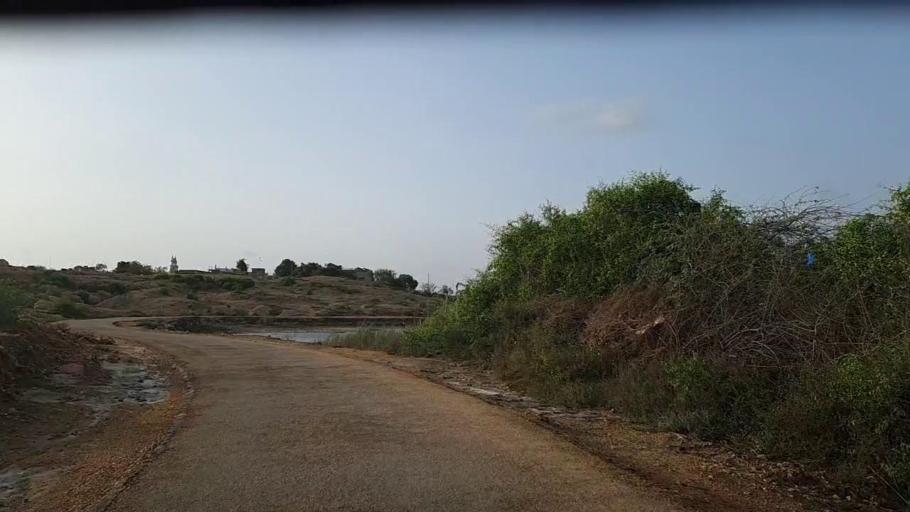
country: PK
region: Sindh
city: Thatta
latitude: 24.7576
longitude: 67.9042
